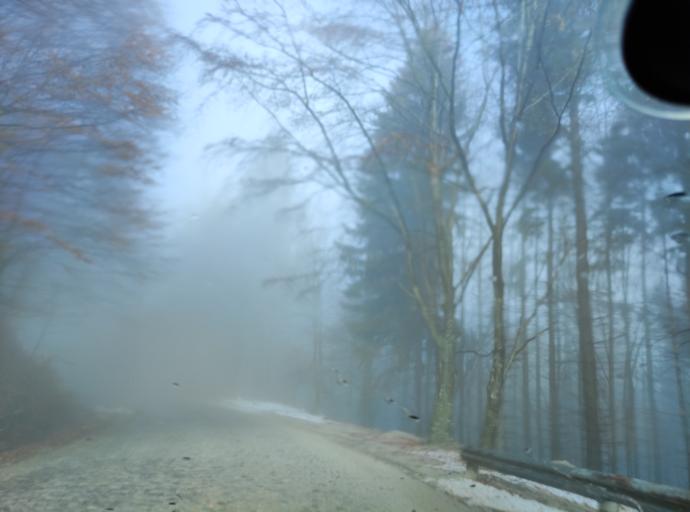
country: BG
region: Sofia-Capital
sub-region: Stolichna Obshtina
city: Sofia
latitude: 42.6104
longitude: 23.2968
